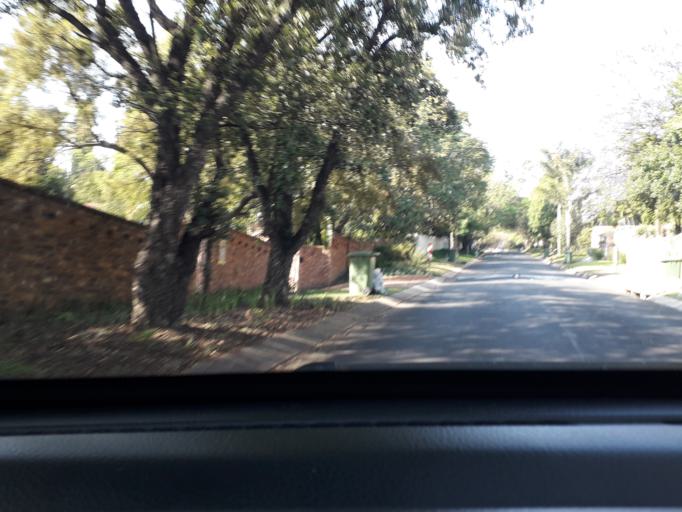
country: ZA
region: Gauteng
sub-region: City of Johannesburg Metropolitan Municipality
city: Midrand
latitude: -26.0737
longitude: 28.0510
